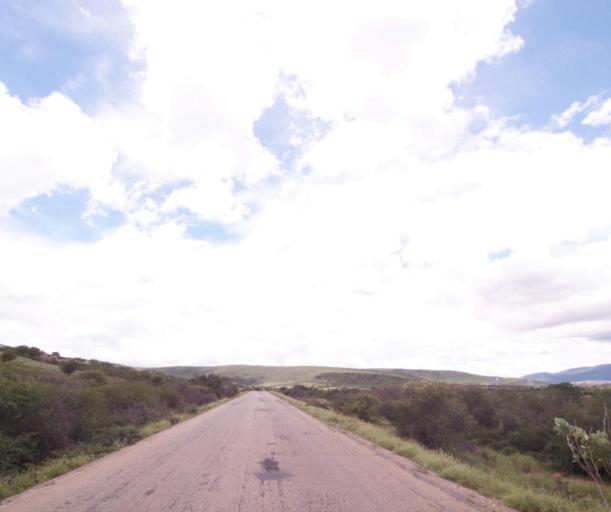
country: BR
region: Bahia
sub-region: Brumado
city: Brumado
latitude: -14.1928
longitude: -41.5795
